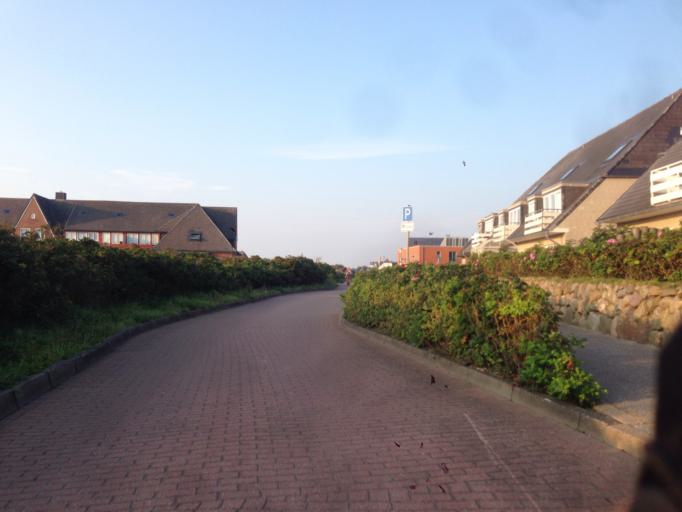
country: DE
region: Schleswig-Holstein
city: Westerland
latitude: 54.9133
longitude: 8.3031
